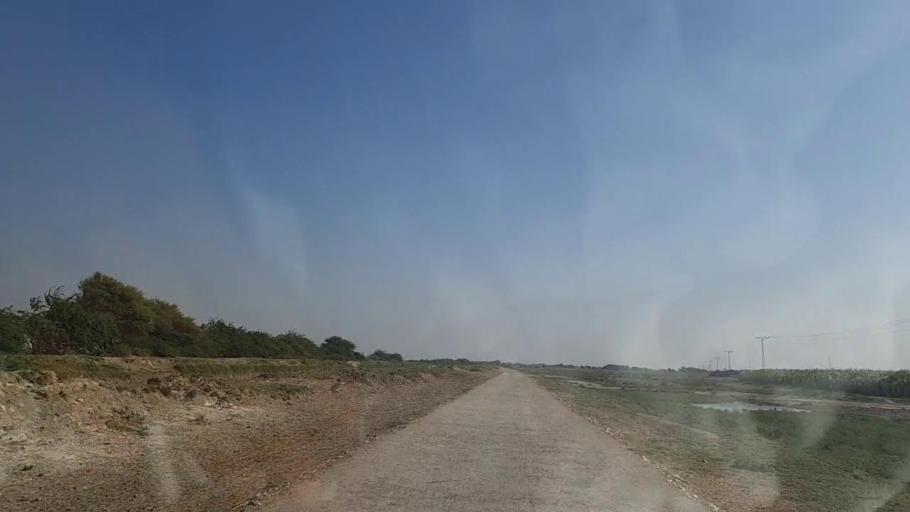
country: PK
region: Sindh
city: Mirpur Batoro
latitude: 24.6112
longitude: 68.1685
